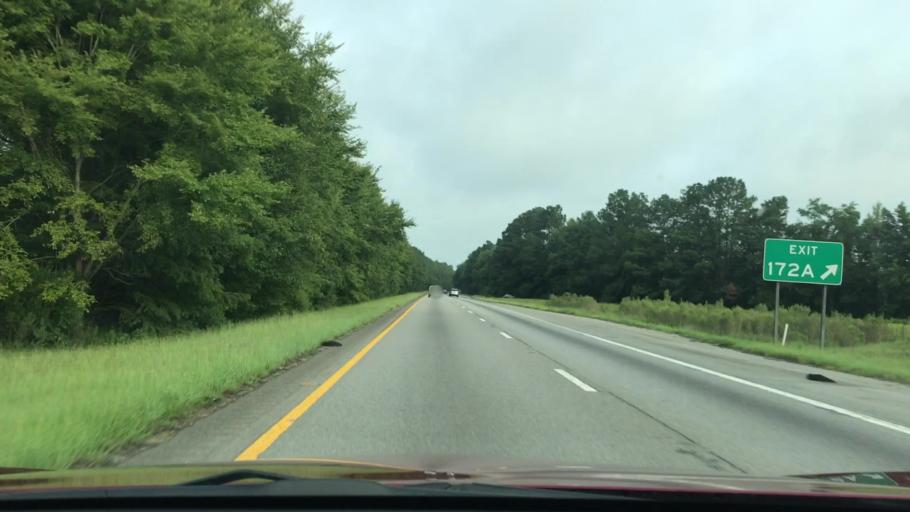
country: US
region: South Carolina
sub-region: Orangeburg County
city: Holly Hill
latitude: 33.2874
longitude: -80.5141
